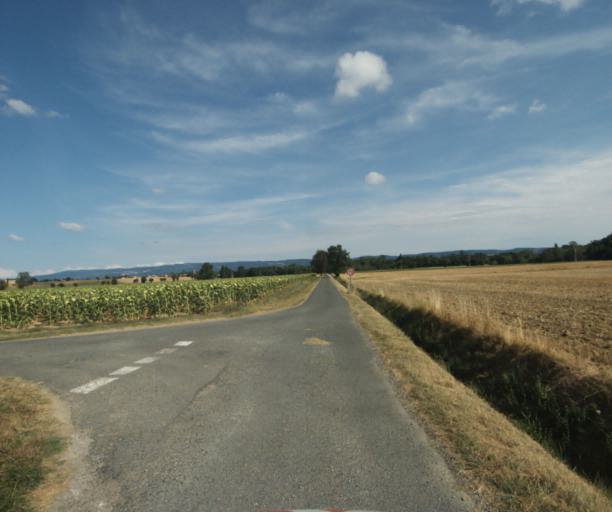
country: FR
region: Midi-Pyrenees
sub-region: Departement de la Haute-Garonne
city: Revel
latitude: 43.5098
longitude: 1.9816
